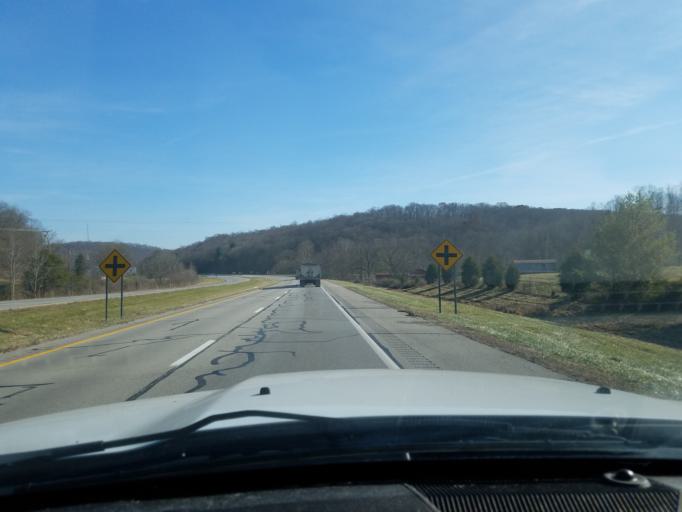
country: US
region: Ohio
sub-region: Pike County
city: Piketon
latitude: 39.0600
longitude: -83.0998
